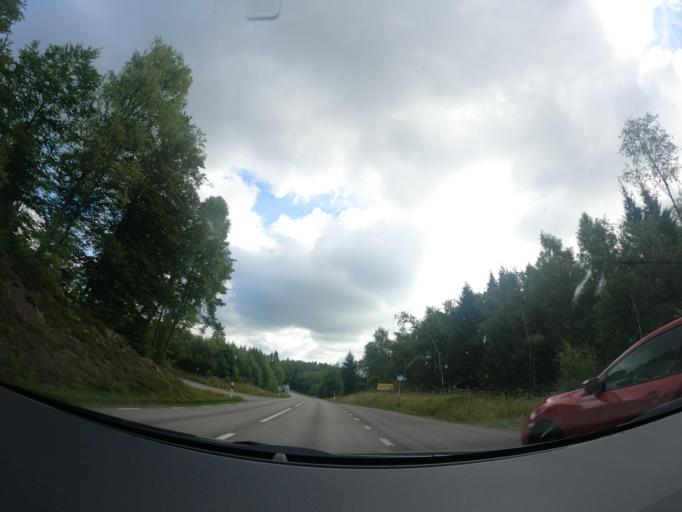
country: SE
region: Halland
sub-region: Hylte Kommun
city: Torup
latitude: 57.1130
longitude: 12.8996
